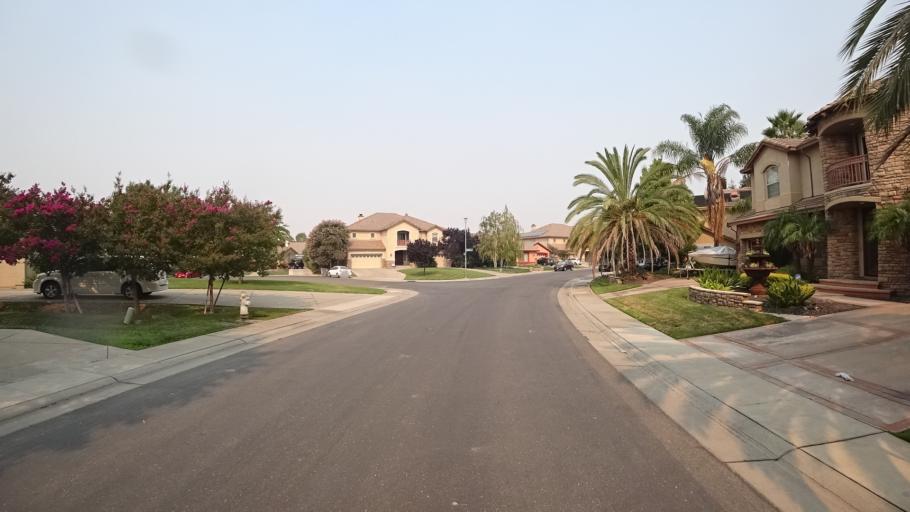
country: US
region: California
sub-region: Sacramento County
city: Laguna
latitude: 38.3952
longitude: -121.4275
